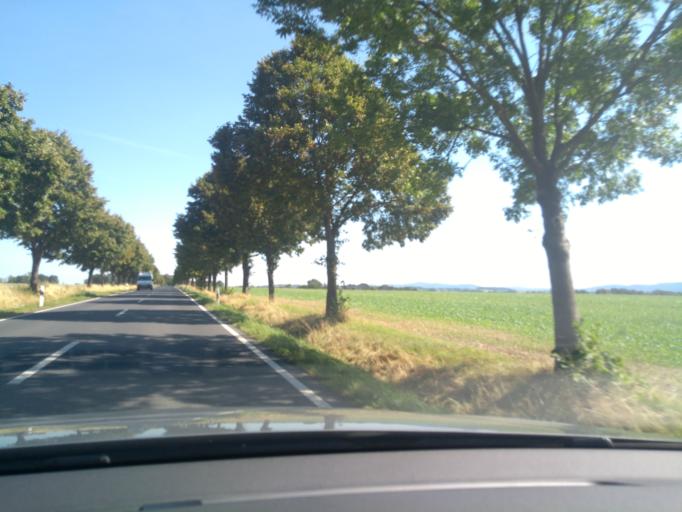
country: DE
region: Saxony
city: Crostwitz
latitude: 51.2138
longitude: 14.2748
